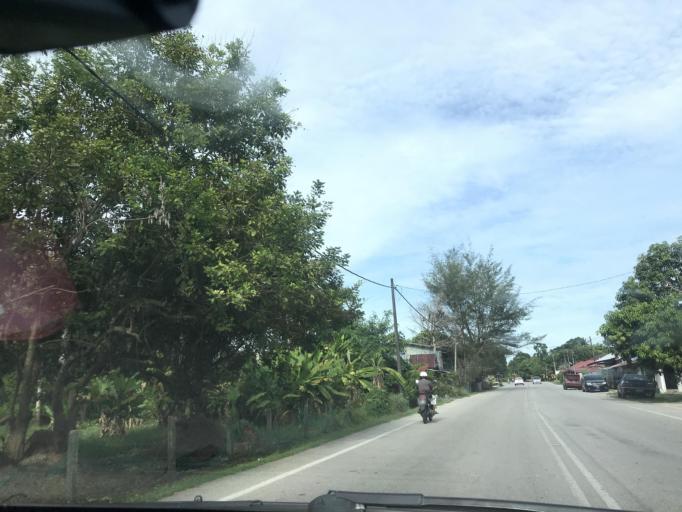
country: MY
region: Kelantan
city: Kota Bharu
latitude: 6.1384
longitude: 102.2083
